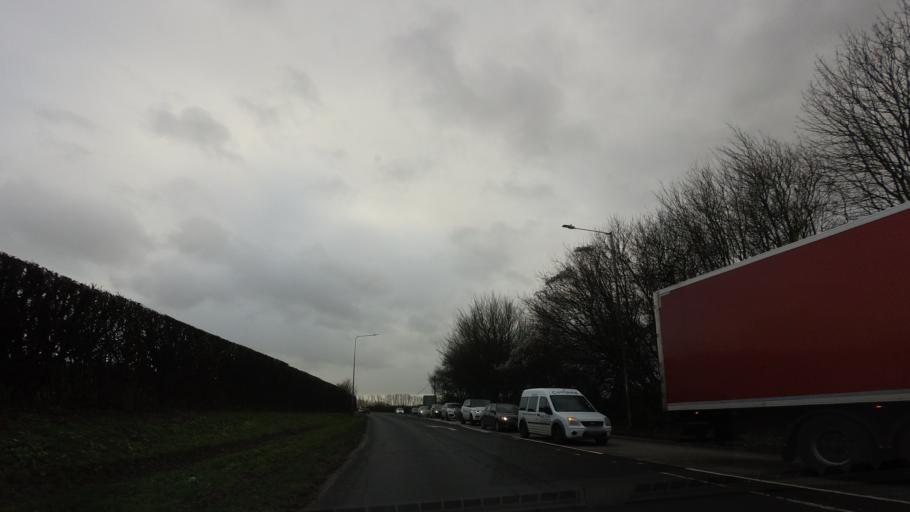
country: GB
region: England
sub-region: Kent
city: Kings Hill
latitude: 51.2509
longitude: 0.3737
